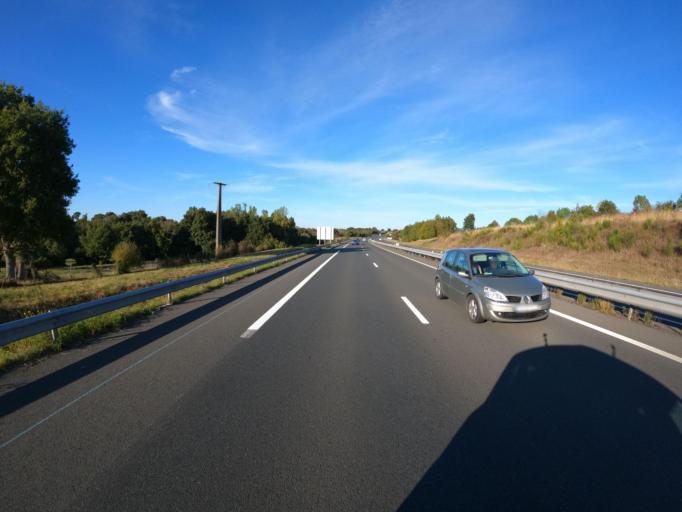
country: FR
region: Pays de la Loire
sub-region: Departement de Maine-et-Loire
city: Chemille-Melay
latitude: 47.2231
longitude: -0.7593
